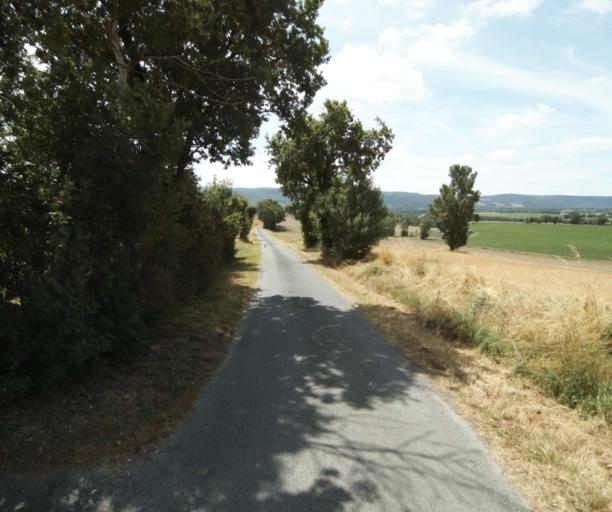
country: FR
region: Midi-Pyrenees
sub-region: Departement du Tarn
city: Dourgne
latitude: 43.4997
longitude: 2.0960
